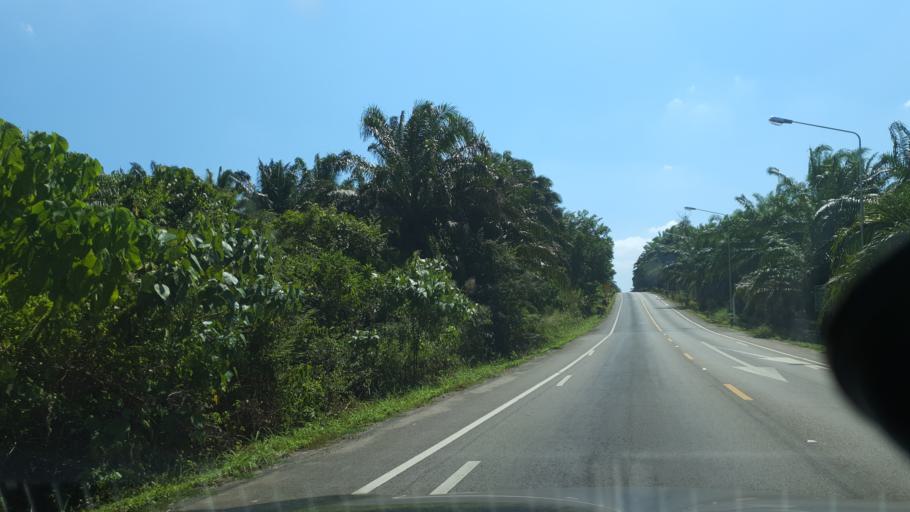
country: TH
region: Krabi
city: Khlong Thom
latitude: 7.9461
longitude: 99.2152
